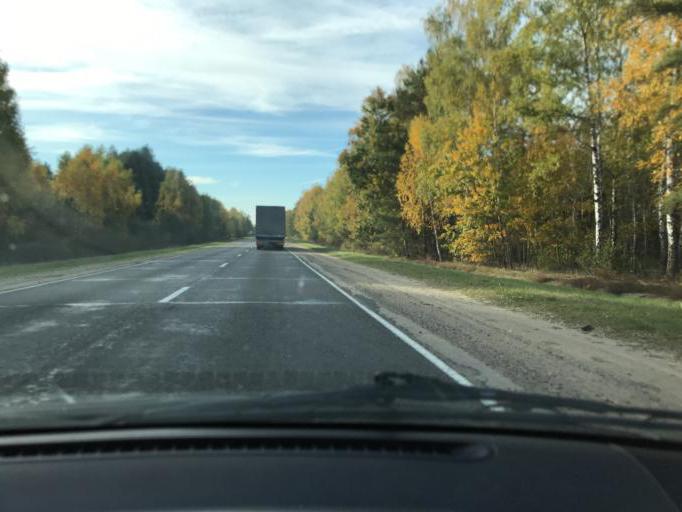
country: BY
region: Brest
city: Horad Pinsk
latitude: 52.1513
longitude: 25.8446
